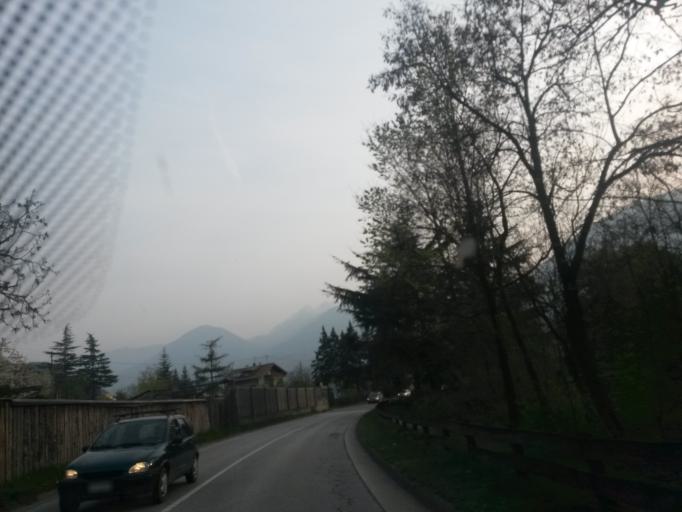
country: IT
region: Trentino-Alto Adige
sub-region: Bolzano
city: Sinigo
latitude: 46.6548
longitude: 11.1854
